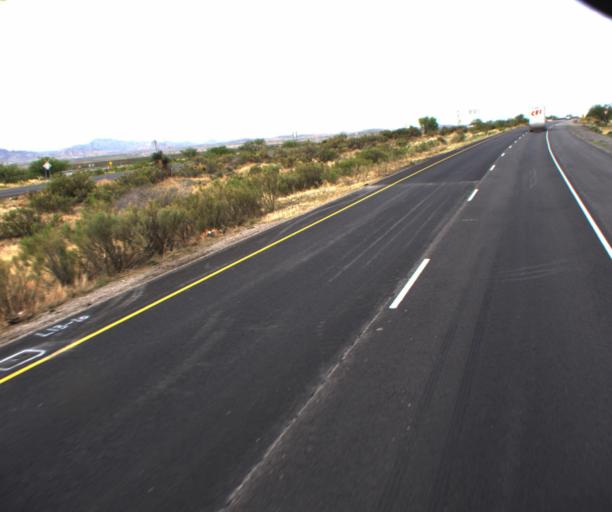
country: US
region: Arizona
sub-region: Cochise County
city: Mescal
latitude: 31.9761
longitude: -110.5090
